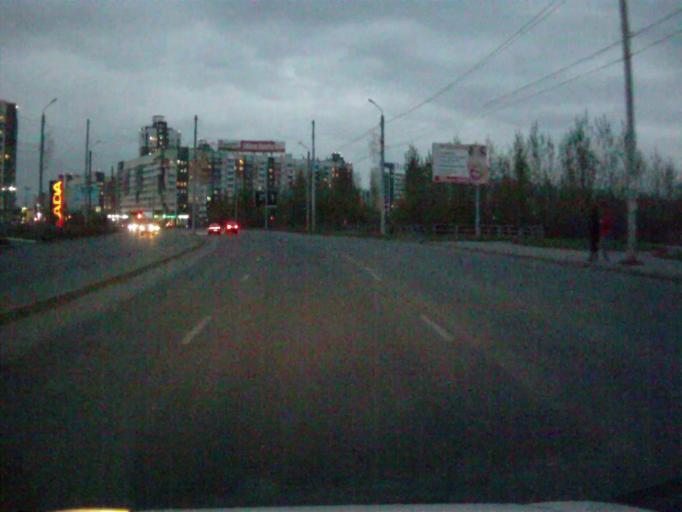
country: RU
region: Chelyabinsk
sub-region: Gorod Chelyabinsk
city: Chelyabinsk
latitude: 55.1693
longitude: 61.2957
